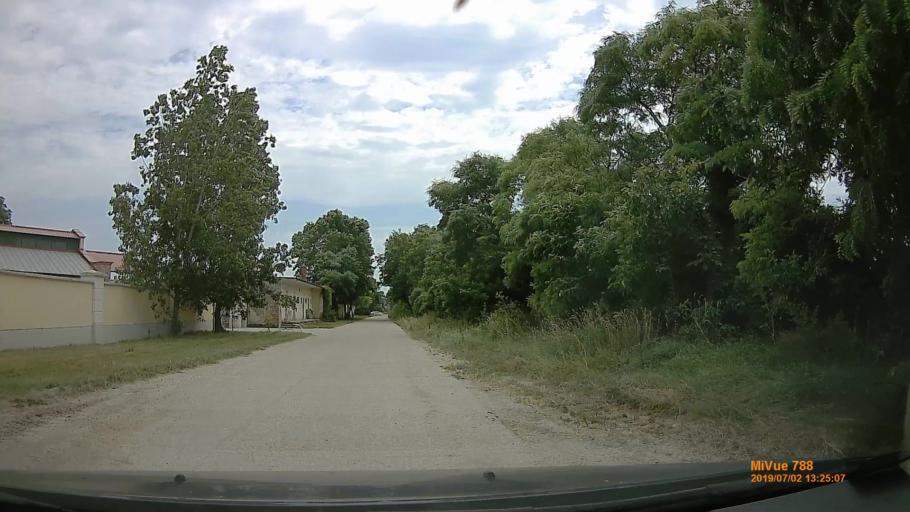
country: HU
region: Gyor-Moson-Sopron
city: Halaszi
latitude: 47.8625
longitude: 17.3156
